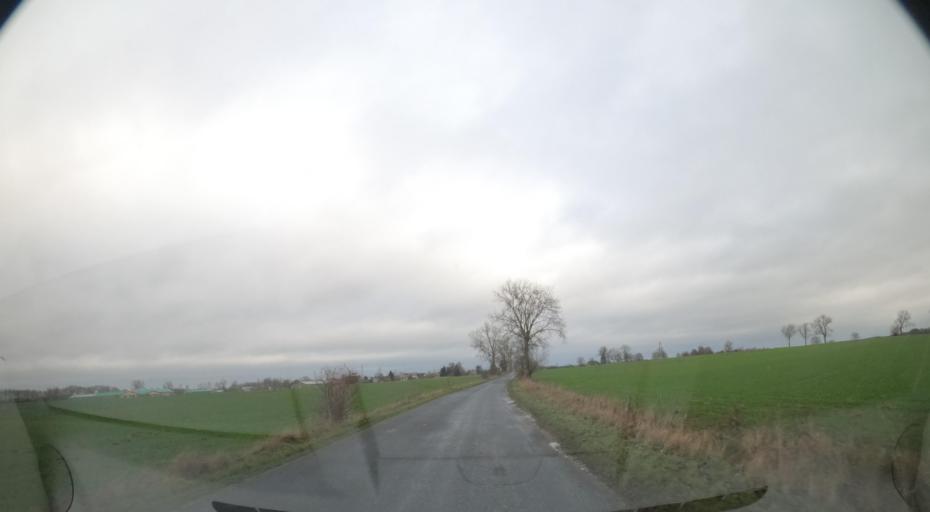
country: PL
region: Greater Poland Voivodeship
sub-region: Powiat pilski
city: Wysoka
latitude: 53.2543
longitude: 17.1507
